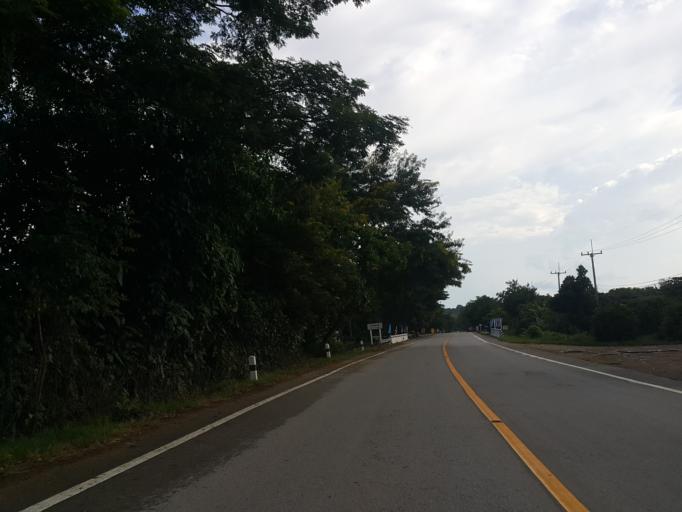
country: TH
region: Chiang Mai
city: Phrao
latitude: 19.2401
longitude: 99.1861
